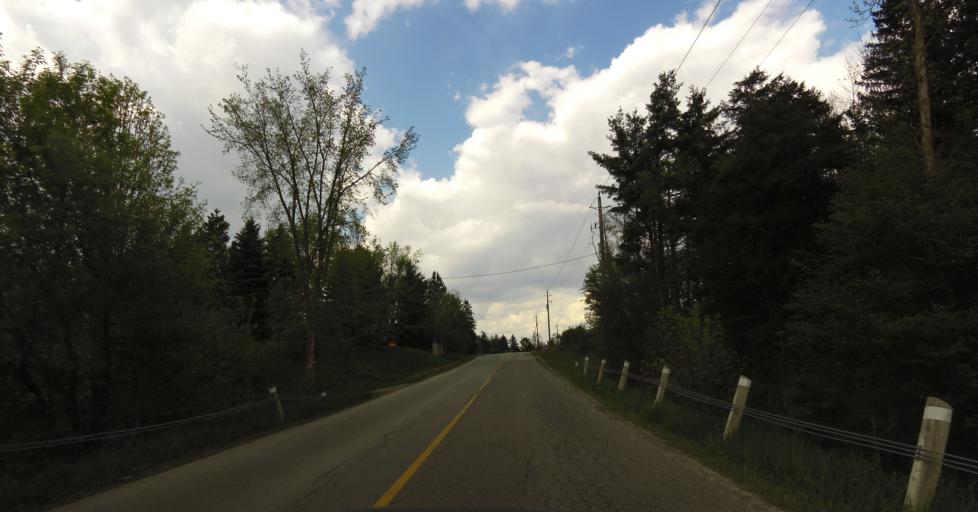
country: CA
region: Ontario
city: Brampton
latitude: 43.7667
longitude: -79.8375
